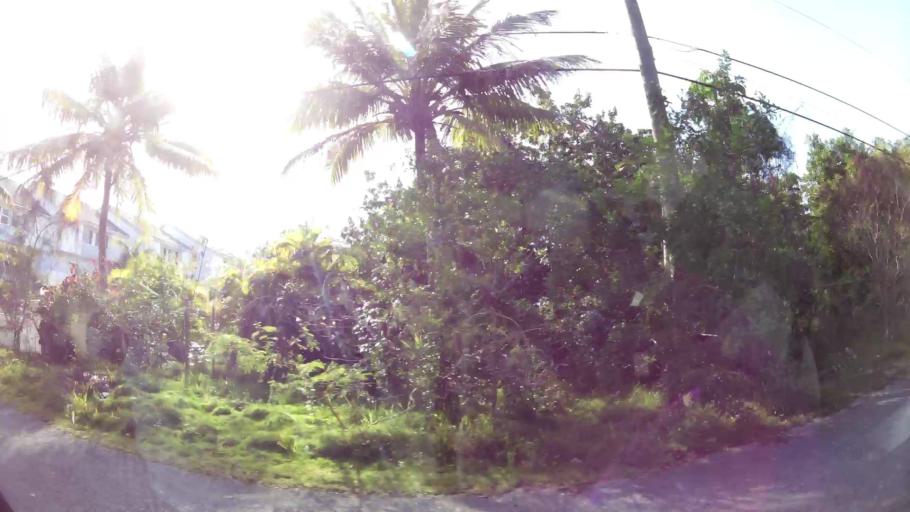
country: BS
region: Freeport
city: Lucaya
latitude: 26.5049
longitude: -78.6587
